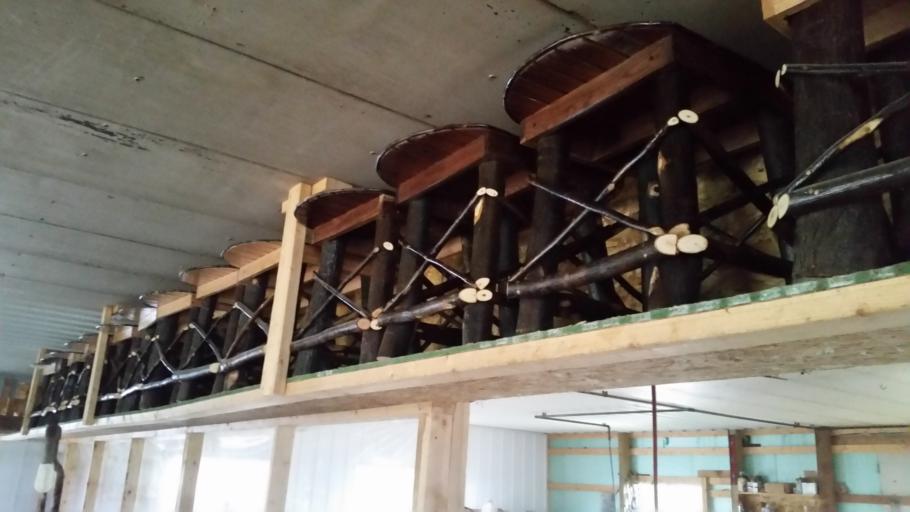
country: US
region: Ohio
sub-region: Holmes County
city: Millersburg
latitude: 40.5703
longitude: -81.7869
